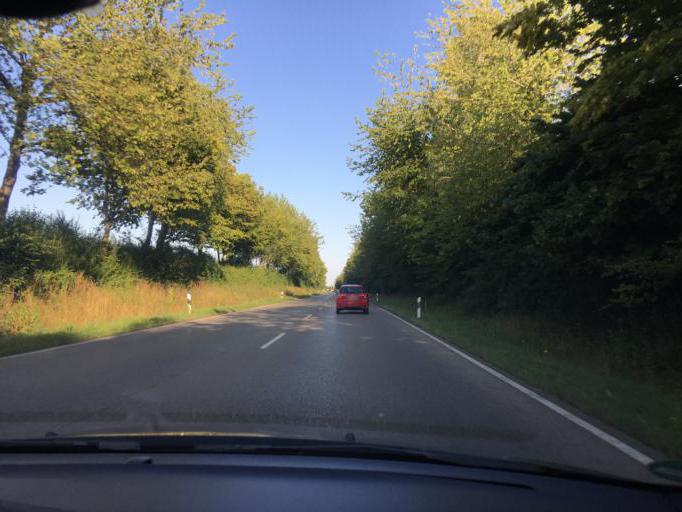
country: DE
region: Bavaria
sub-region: Upper Bavaria
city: Stammham
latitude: 48.2845
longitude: 11.8862
